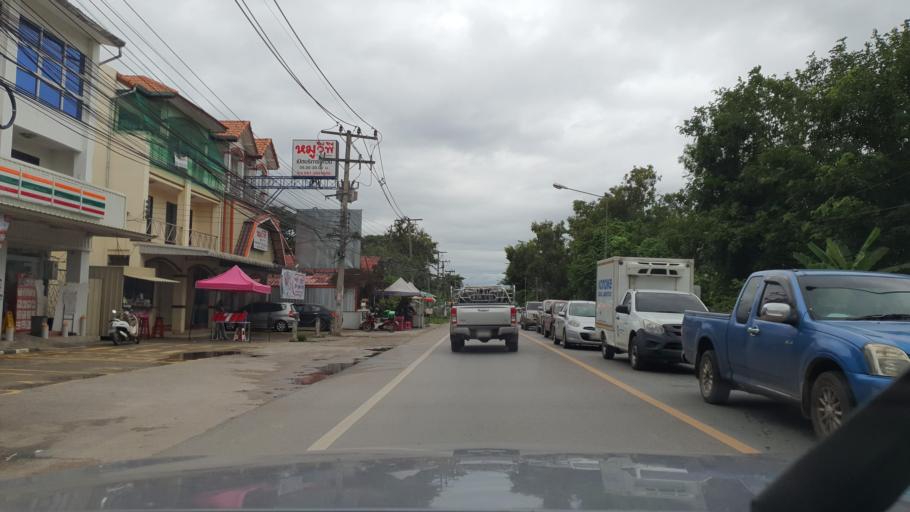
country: TH
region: Lamphun
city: Lamphun
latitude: 18.5844
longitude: 98.9923
